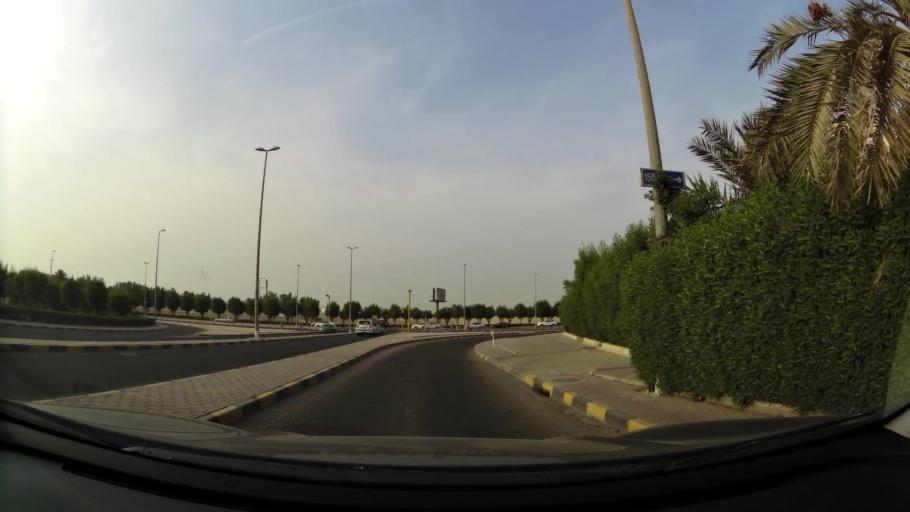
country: KW
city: Al Funaytis
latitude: 29.2210
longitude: 48.0753
